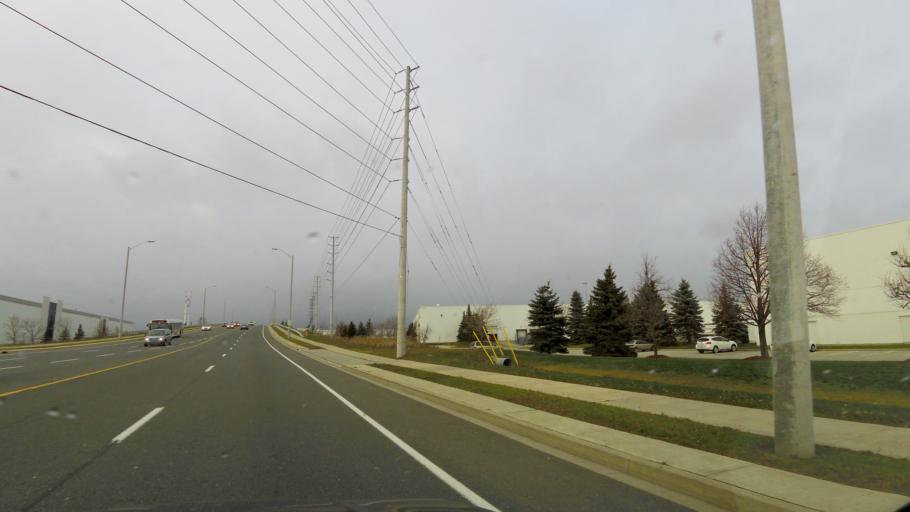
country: CA
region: Ontario
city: Mississauga
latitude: 43.6216
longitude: -79.6967
